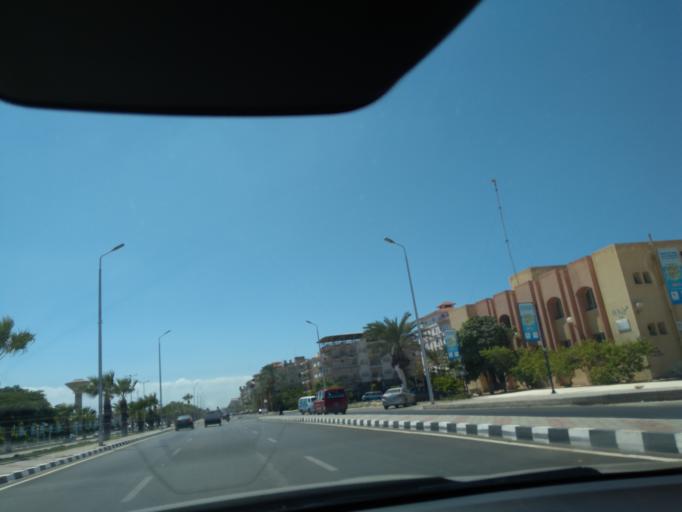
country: EG
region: Dumyat
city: Faraskur
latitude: 31.4431
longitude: 31.6896
